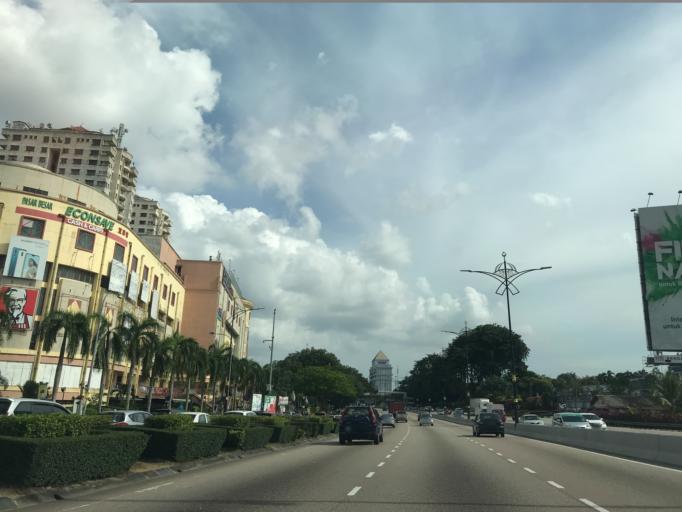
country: MY
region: Johor
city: Skudai
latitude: 1.5422
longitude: 103.6588
